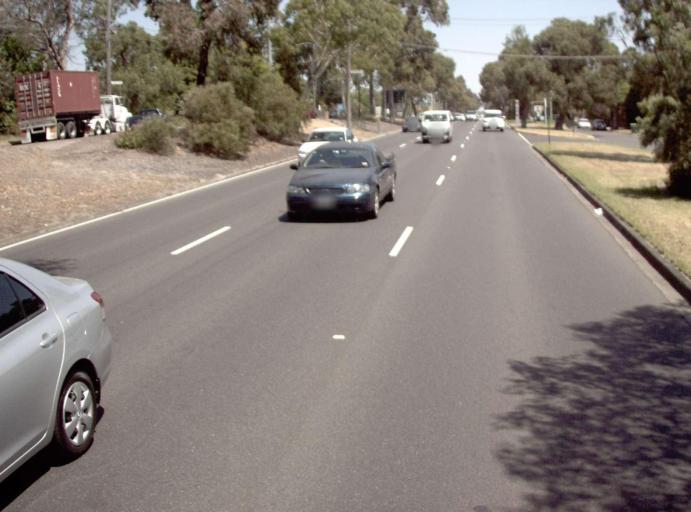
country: AU
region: Victoria
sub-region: Whitehorse
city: Forest Hill
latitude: -37.8365
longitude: 145.1721
